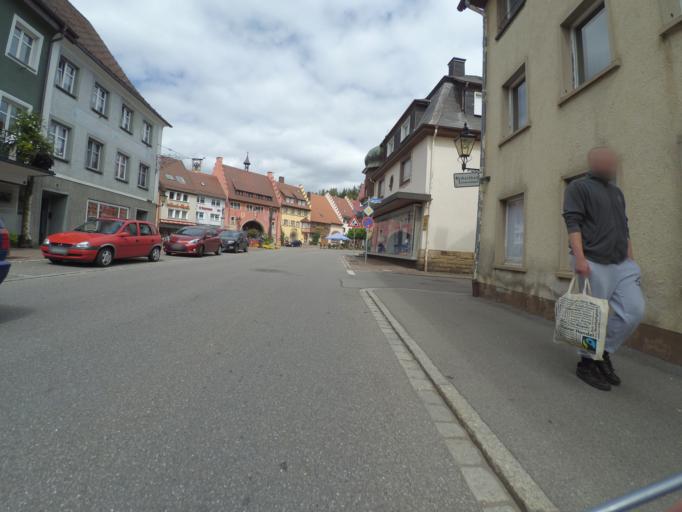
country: DE
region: Baden-Wuerttemberg
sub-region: Freiburg Region
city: Loffingen
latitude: 47.8834
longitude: 8.3439
